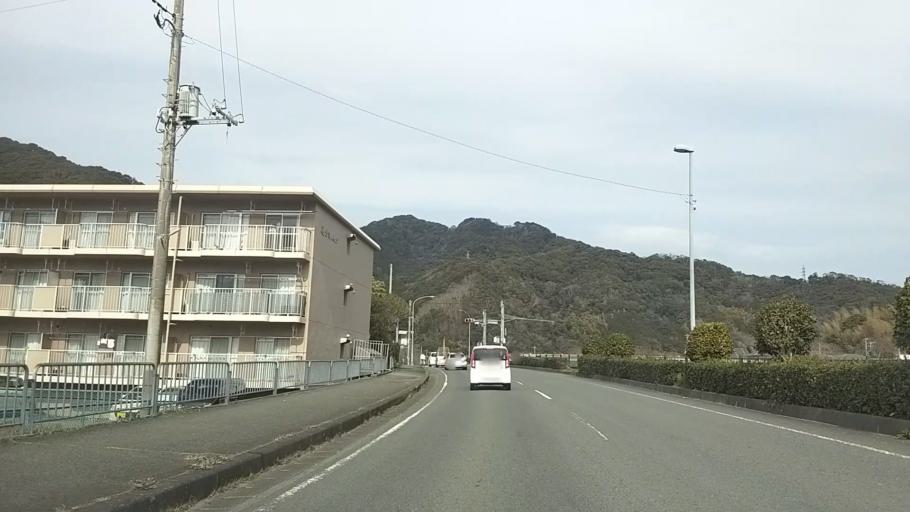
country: JP
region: Shizuoka
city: Shimoda
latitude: 34.7020
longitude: 138.9406
